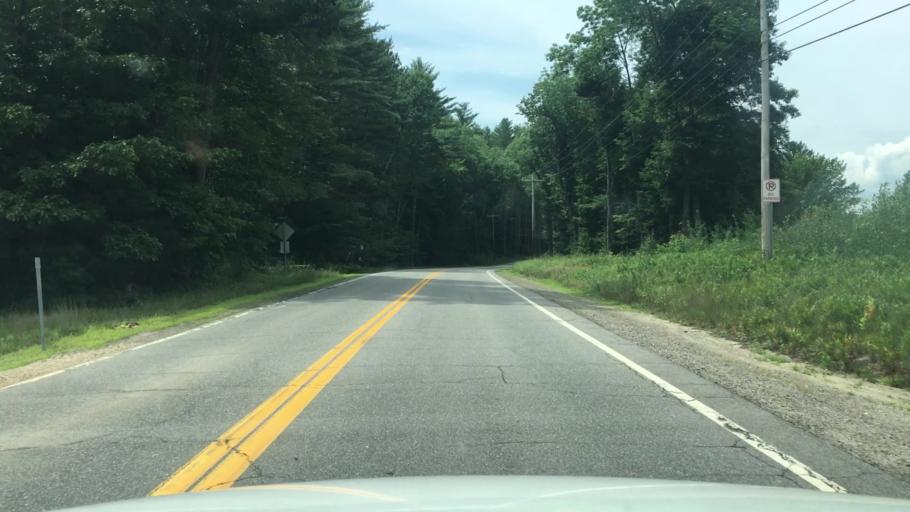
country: US
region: New Hampshire
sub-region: Grafton County
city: Plymouth
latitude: 43.7799
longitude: -71.6662
